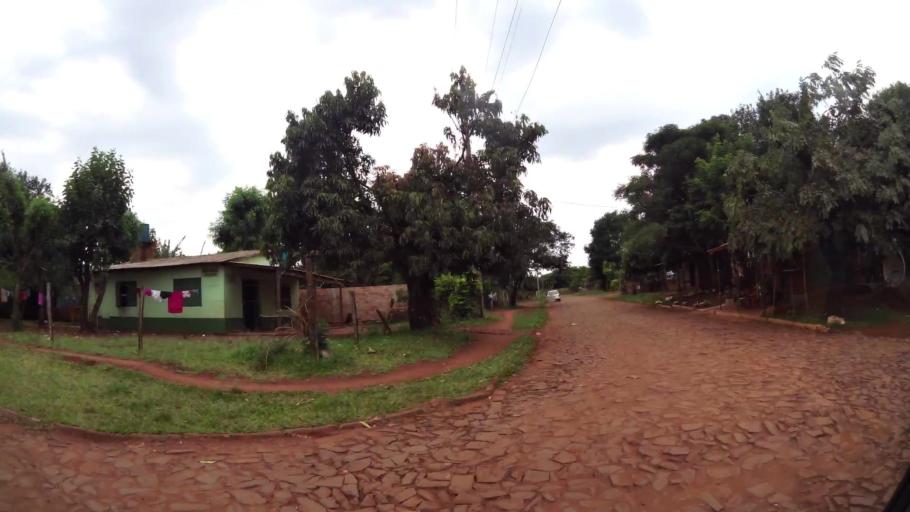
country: PY
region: Alto Parana
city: Presidente Franco
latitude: -25.5505
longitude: -54.6539
